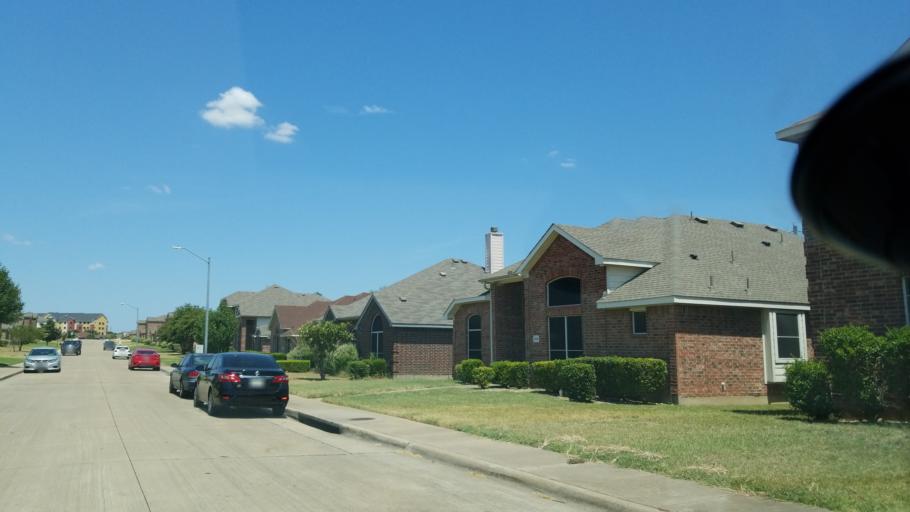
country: US
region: Texas
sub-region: Dallas County
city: Duncanville
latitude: 32.6401
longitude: -96.8841
